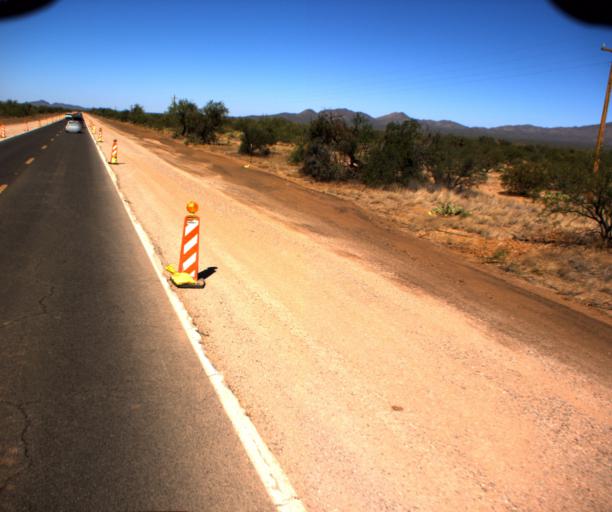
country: US
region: Arizona
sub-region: Pima County
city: Sells
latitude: 31.9855
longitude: -111.7197
